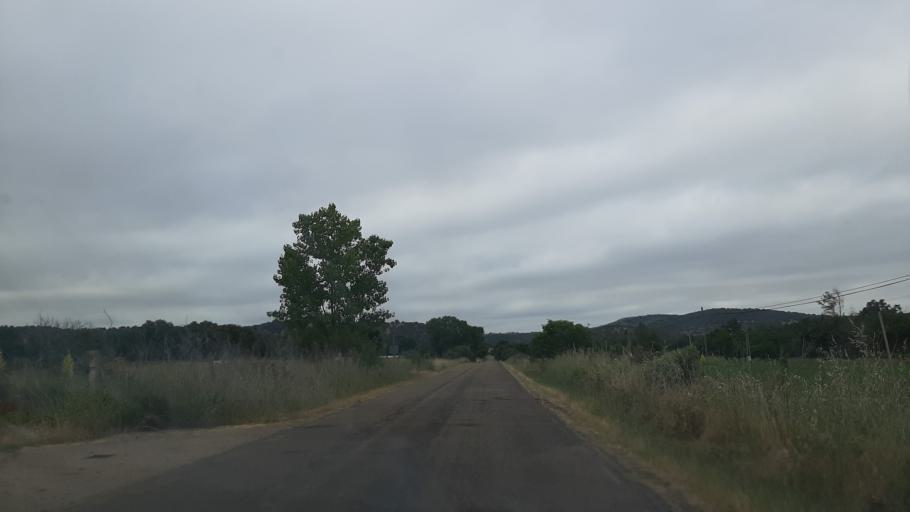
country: ES
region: Castille and Leon
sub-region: Provincia de Salamanca
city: Pastores
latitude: 40.5633
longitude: -6.4855
